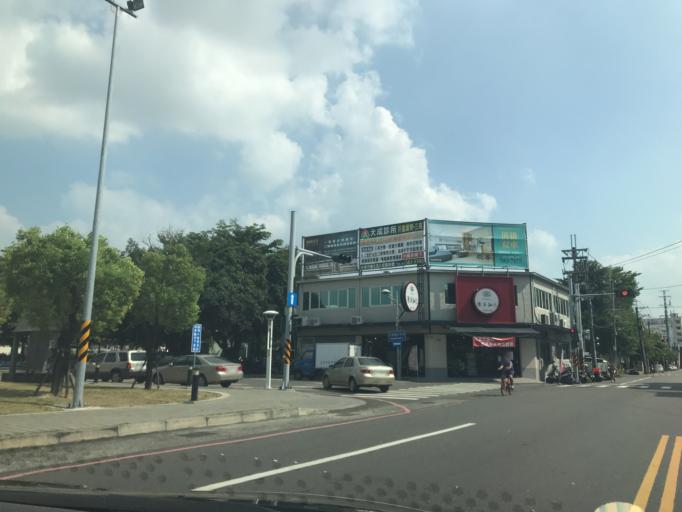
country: TW
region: Taiwan
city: Yujing
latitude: 23.1333
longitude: 120.3057
